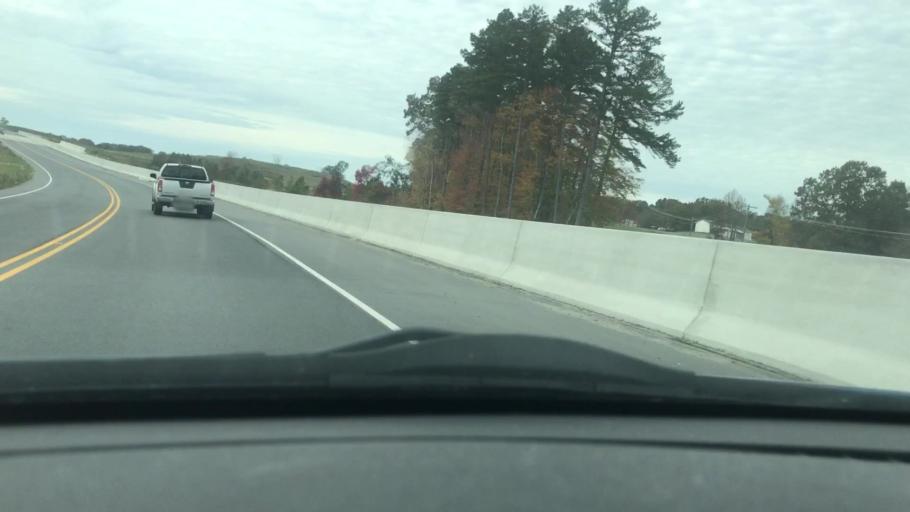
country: US
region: North Carolina
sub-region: Randolph County
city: Asheboro
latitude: 35.6973
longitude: -79.8651
